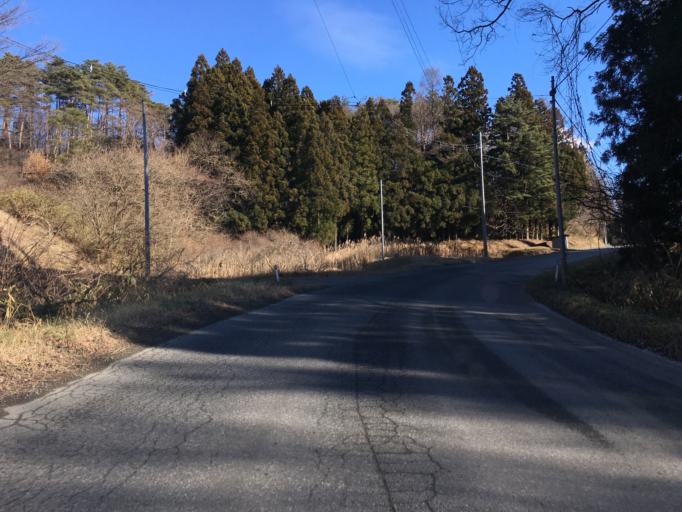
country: JP
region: Fukushima
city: Ishikawa
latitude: 37.2148
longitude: 140.5445
